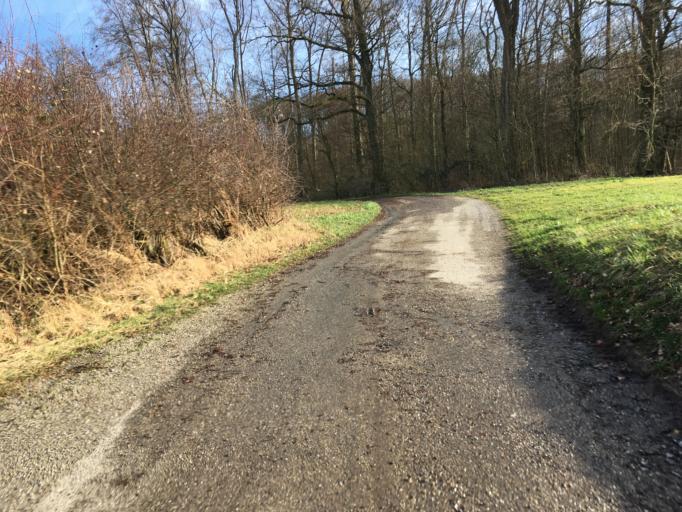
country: DE
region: Baden-Wuerttemberg
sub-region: Regierungsbezirk Stuttgart
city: Lehrensteinsfeld
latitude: 49.1256
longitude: 9.3402
